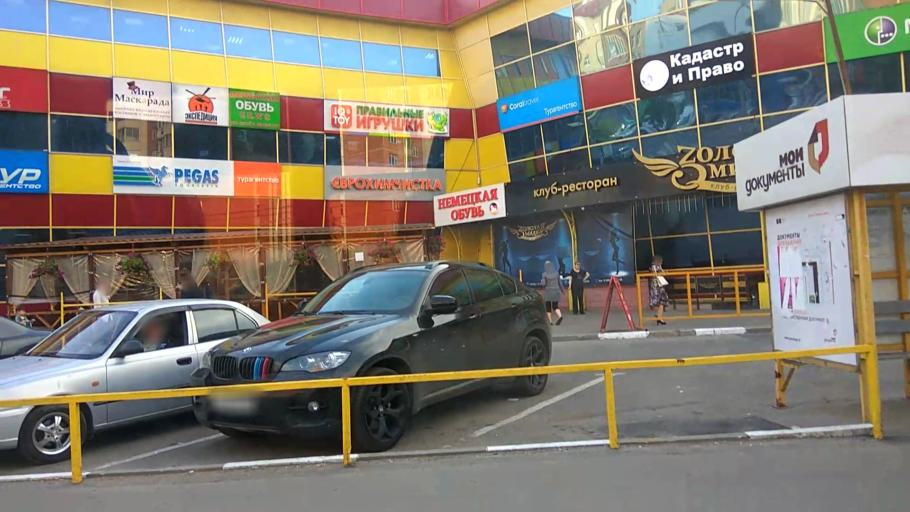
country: RU
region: Moskovskaya
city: Yubileyny
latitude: 55.9144
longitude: 37.8672
